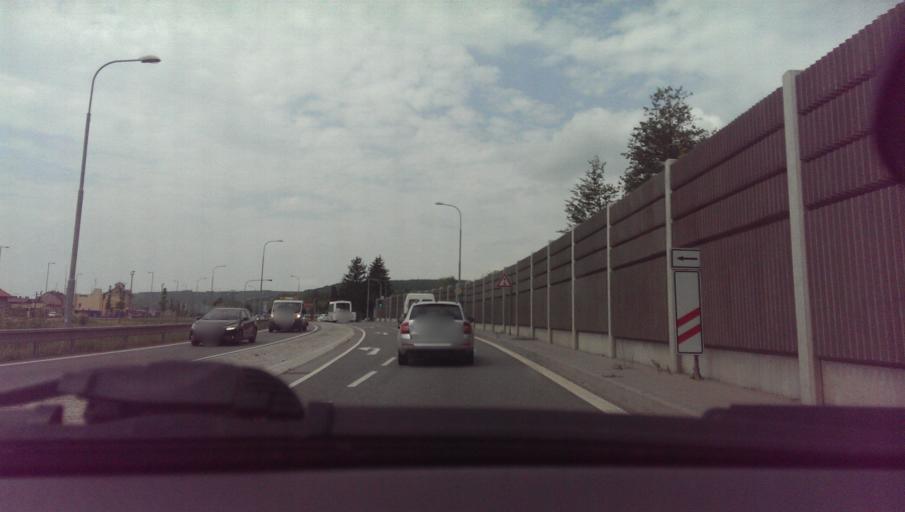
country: CZ
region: South Moravian
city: Nesovice
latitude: 49.1500
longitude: 17.0841
